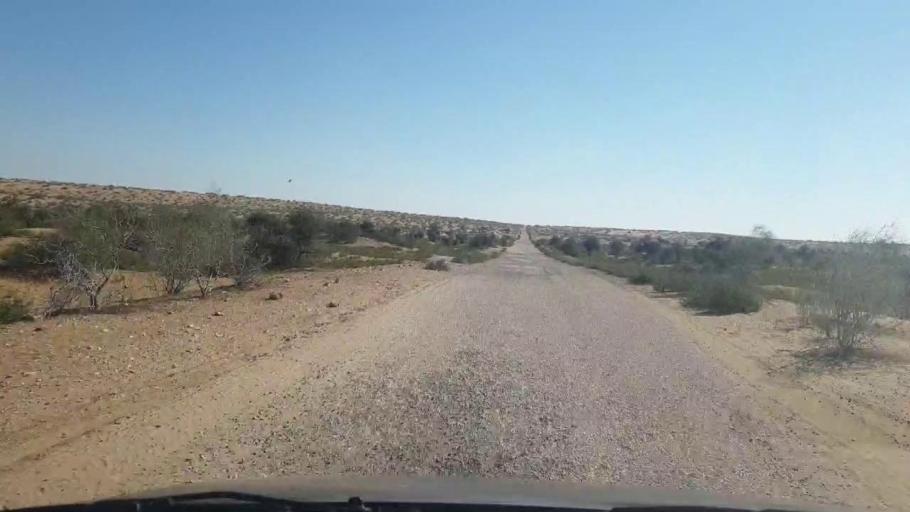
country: PK
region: Sindh
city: Bozdar
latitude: 27.0097
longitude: 68.7982
